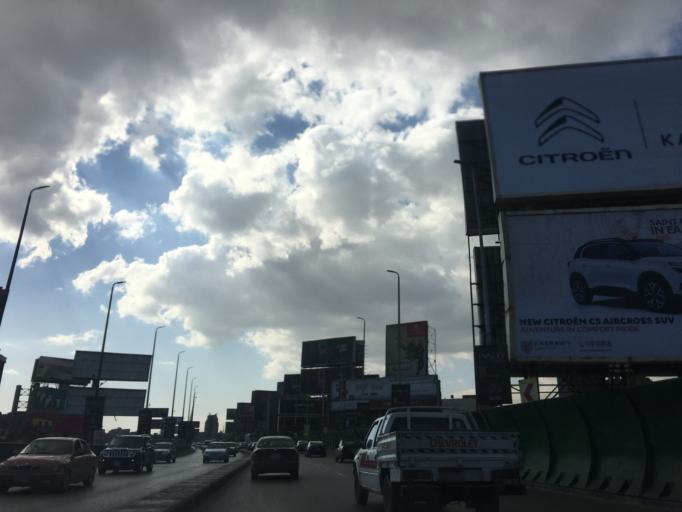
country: EG
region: Muhafazat al Qahirah
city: Cairo
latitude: 30.0742
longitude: 31.2716
